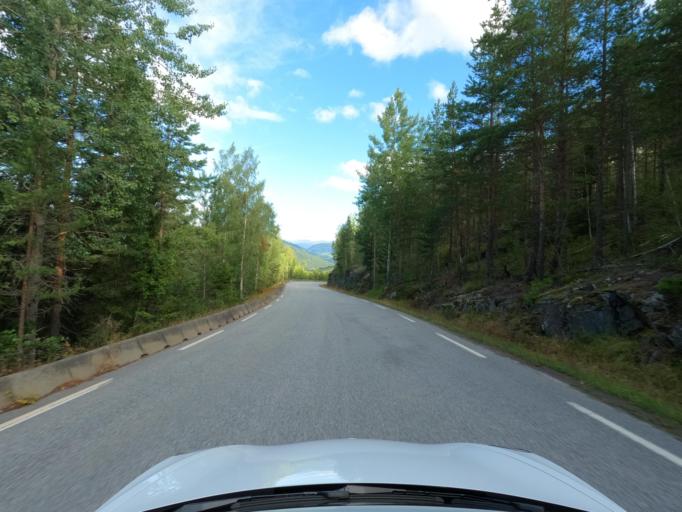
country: NO
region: Telemark
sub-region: Tinn
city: Rjukan
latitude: 59.9780
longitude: 8.8559
